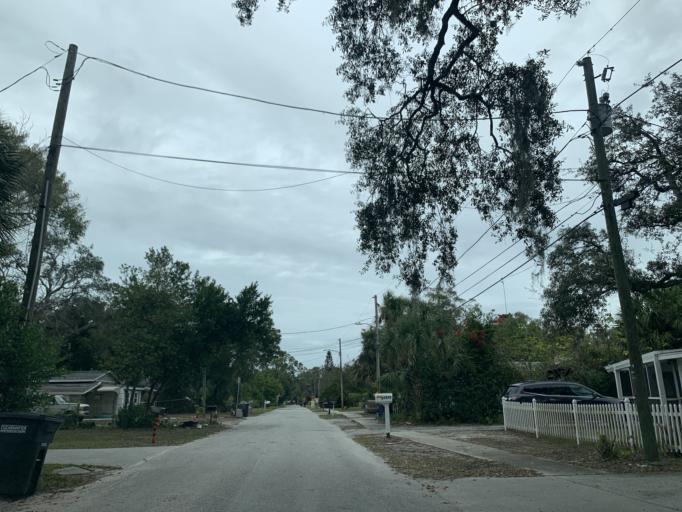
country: US
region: Florida
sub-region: Pinellas County
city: Belleair
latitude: 27.9395
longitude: -82.7899
